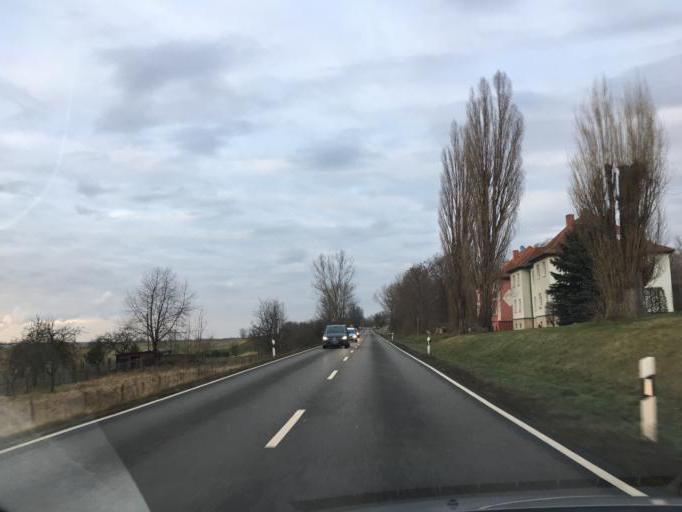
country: DE
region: Saxony
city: Regis-Breitingen
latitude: 51.0760
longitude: 12.4641
